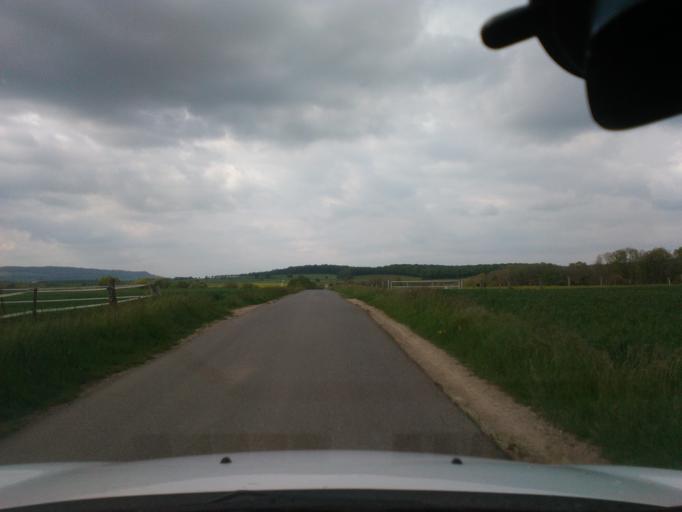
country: FR
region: Lorraine
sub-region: Departement des Vosges
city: Mirecourt
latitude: 48.3389
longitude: 6.1009
